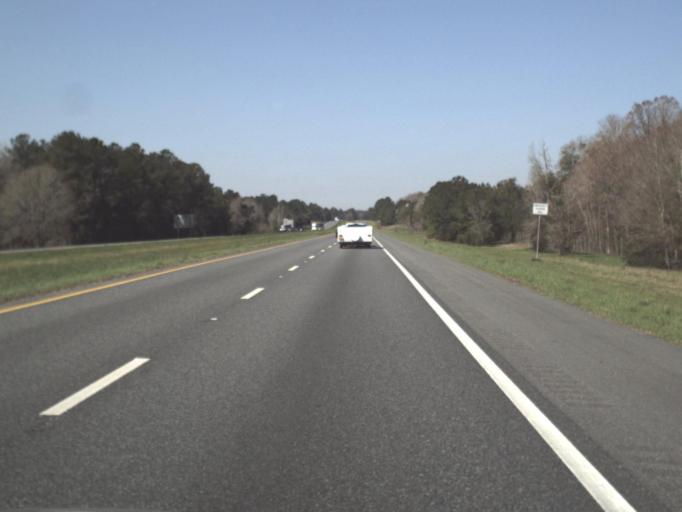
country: US
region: Florida
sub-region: Jackson County
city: Marianna
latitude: 30.7257
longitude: -85.2050
